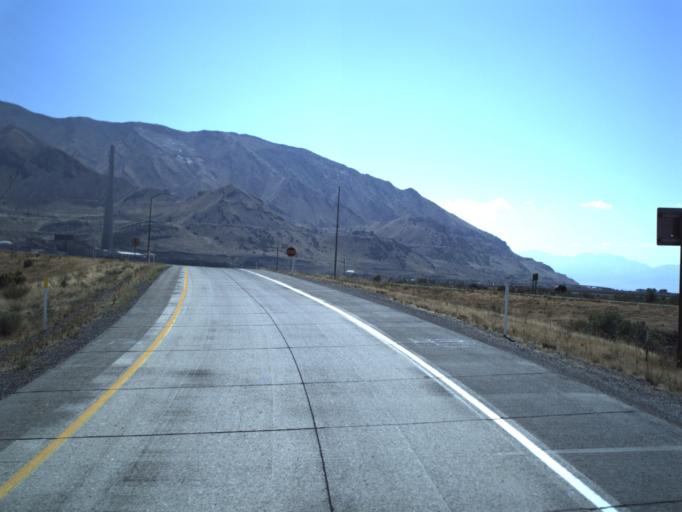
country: US
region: Utah
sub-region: Salt Lake County
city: Magna
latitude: 40.7472
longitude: -112.1837
